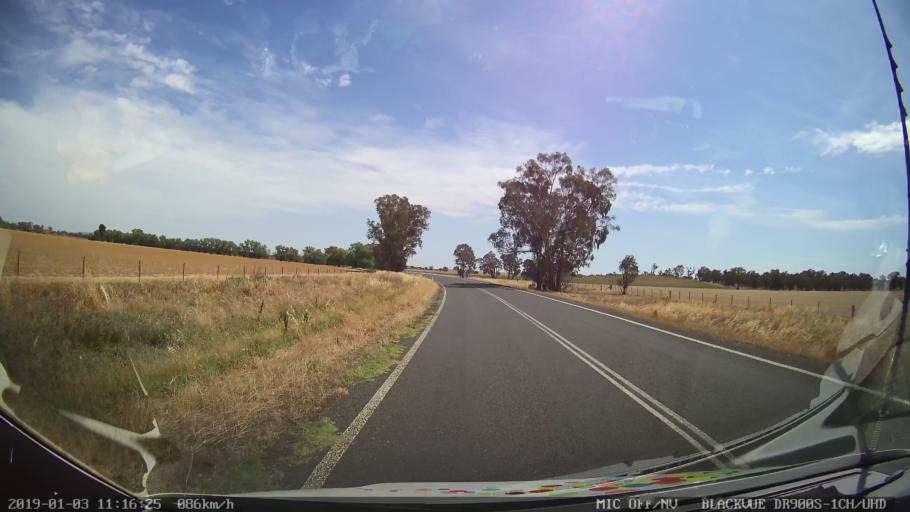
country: AU
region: New South Wales
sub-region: Young
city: Young
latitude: -34.1521
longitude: 148.2697
